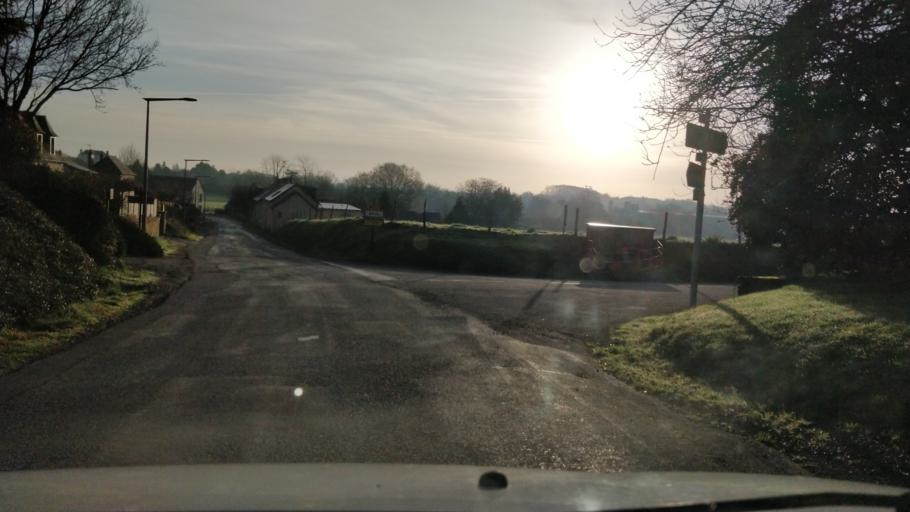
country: FR
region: Brittany
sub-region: Departement d'Ille-et-Vilaine
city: Bais
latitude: 48.0087
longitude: -1.2965
